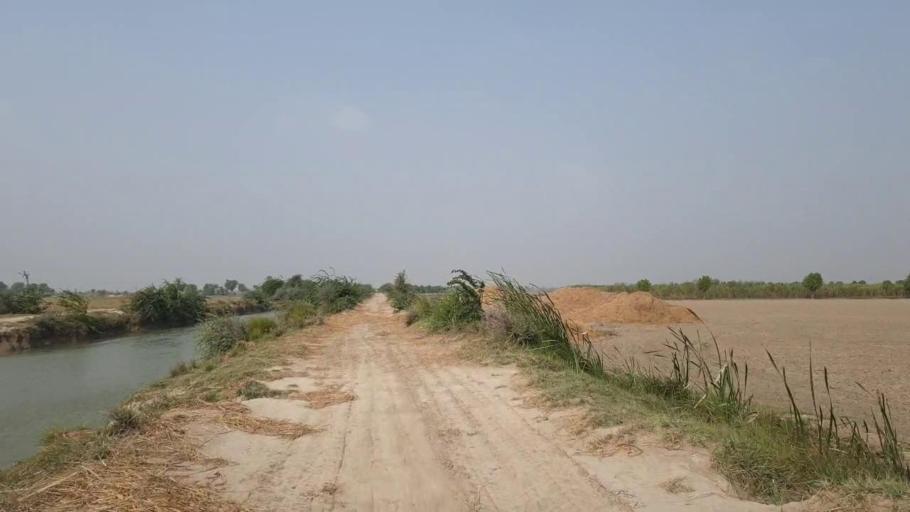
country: PK
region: Sindh
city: Kario
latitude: 24.8495
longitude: 68.5316
